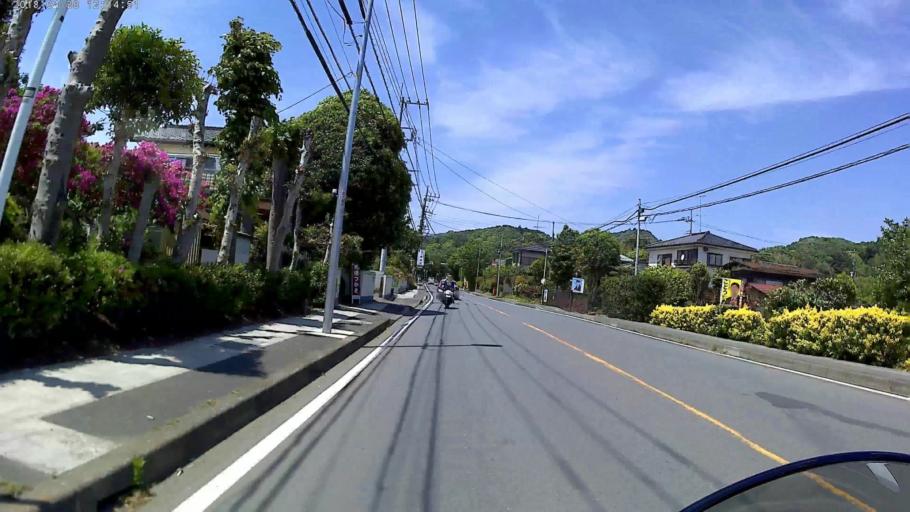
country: JP
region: Kanagawa
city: Zama
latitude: 35.5386
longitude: 139.3056
